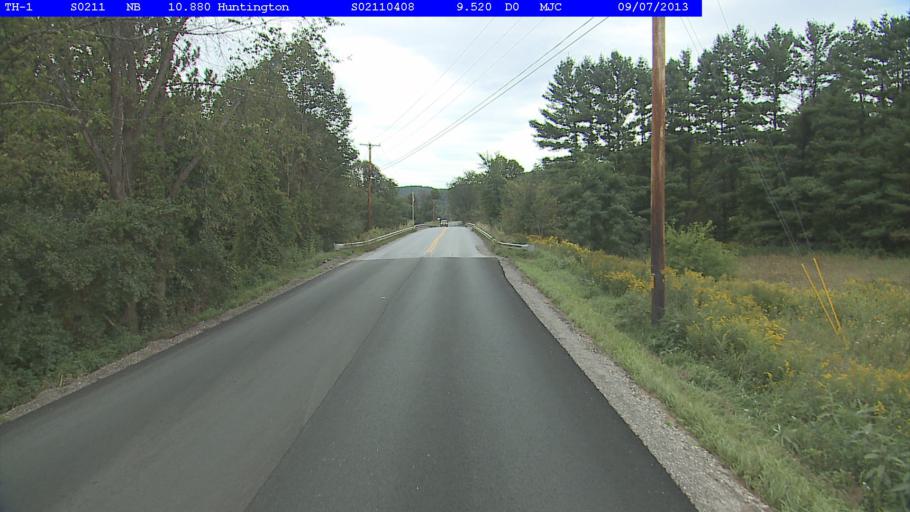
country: US
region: Vermont
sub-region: Chittenden County
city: Williston
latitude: 44.3508
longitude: -72.9924
